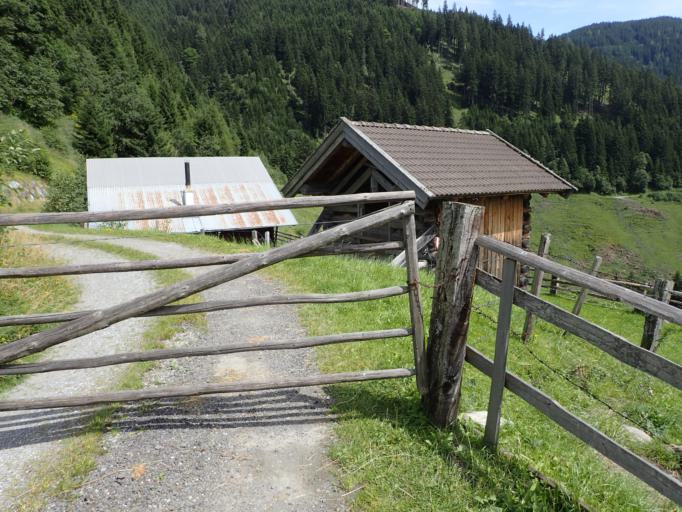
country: AT
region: Salzburg
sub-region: Politischer Bezirk Zell am See
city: Taxenbach
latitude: 47.3274
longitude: 12.9777
